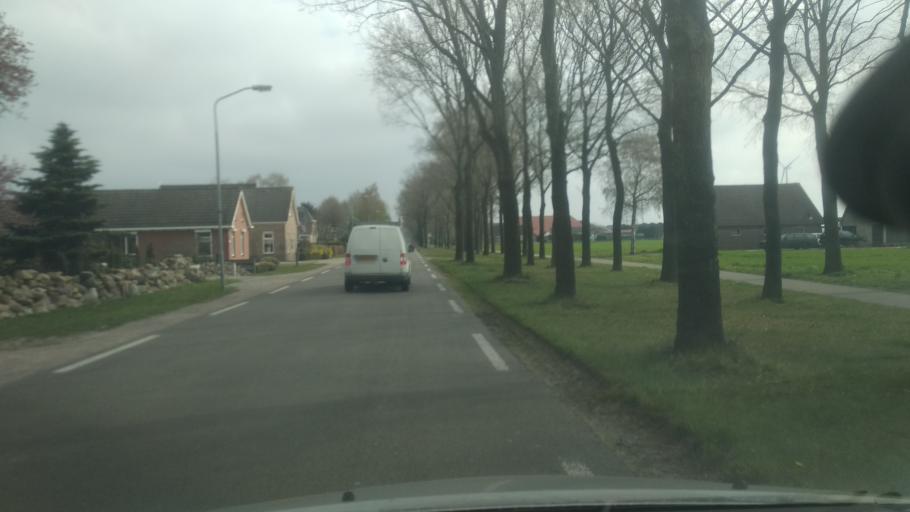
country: NL
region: Groningen
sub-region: Gemeente Stadskanaal
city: Stadskanaal
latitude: 52.9159
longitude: 6.9532
